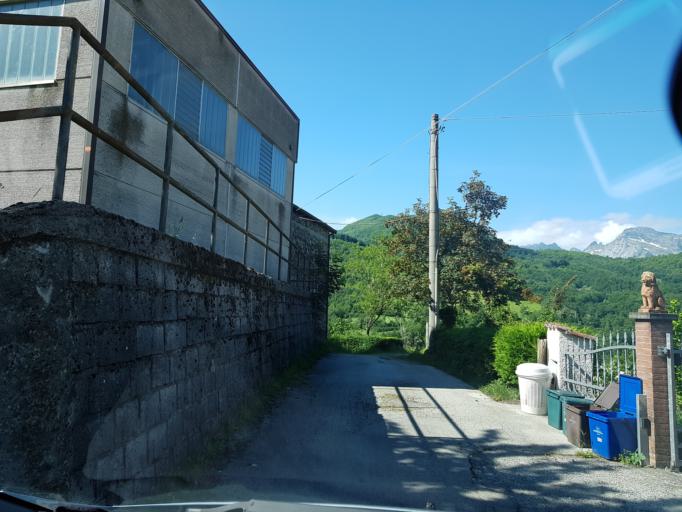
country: IT
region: Tuscany
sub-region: Provincia di Lucca
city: Piazza al Serchio-San Michele
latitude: 44.1828
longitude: 10.3030
